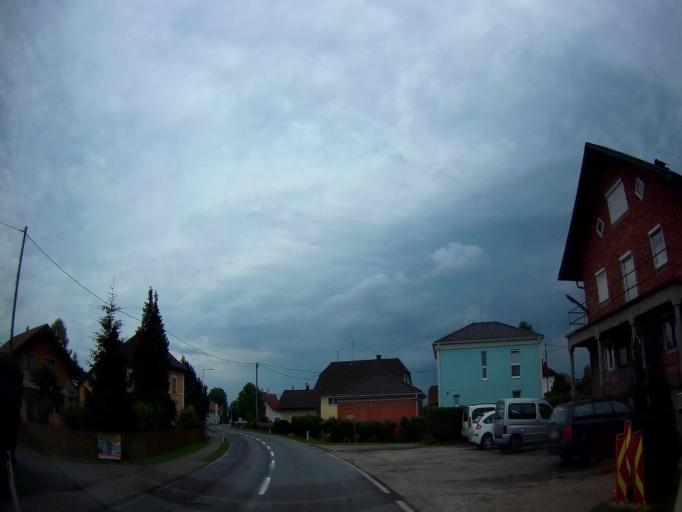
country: AT
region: Upper Austria
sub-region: Politischer Bezirk Braunau am Inn
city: Braunau am Inn
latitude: 48.1510
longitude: 13.1215
